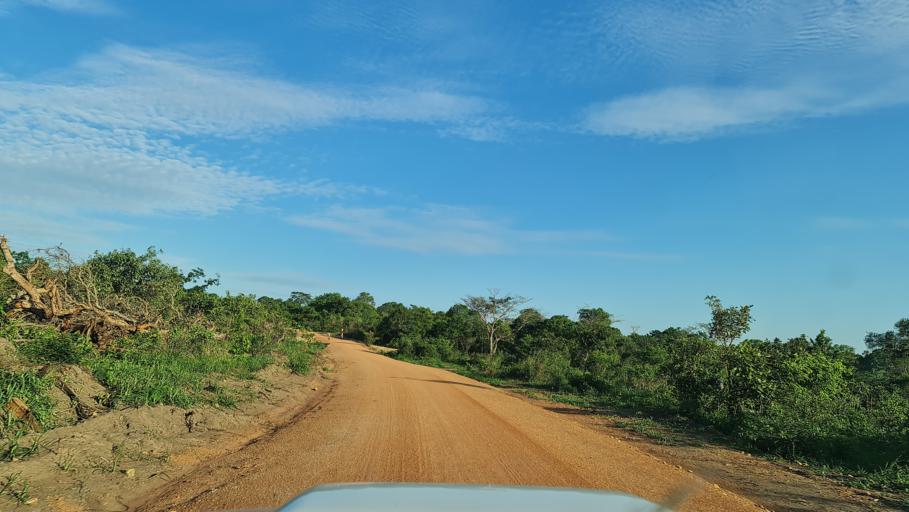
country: MZ
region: Nampula
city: Nacala
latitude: -14.6712
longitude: 40.2732
